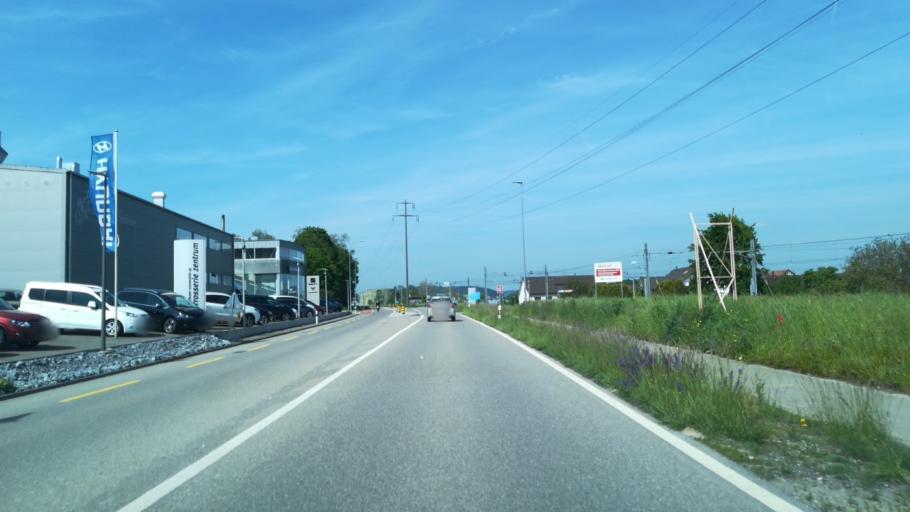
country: CH
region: Thurgau
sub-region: Frauenfeld District
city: Gachnang
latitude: 47.5520
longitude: 8.8642
